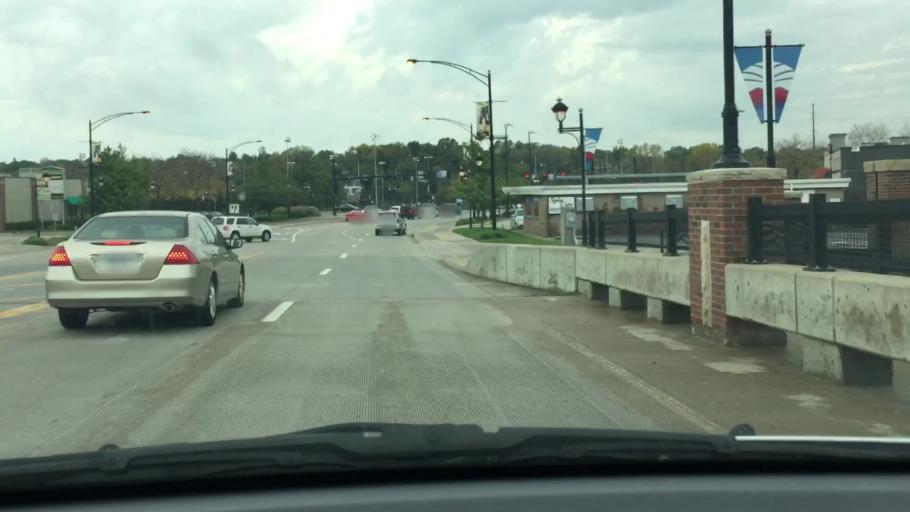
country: US
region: Iowa
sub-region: Johnson County
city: Coralville
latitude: 41.6705
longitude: -91.5656
